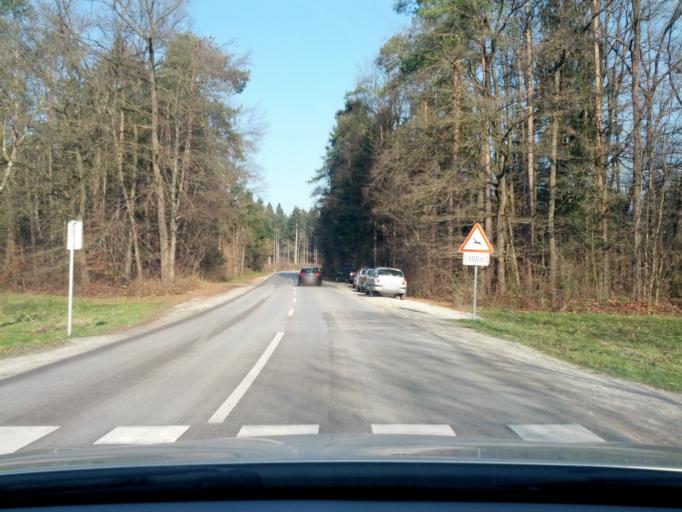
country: SI
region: Ljubljana
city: Ljubljana
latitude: 46.0534
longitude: 14.4617
